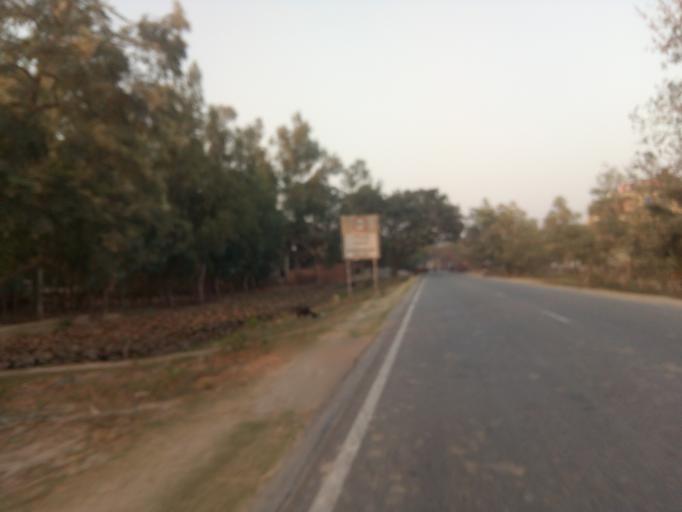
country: BD
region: Rajshahi
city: Bogra
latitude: 24.6433
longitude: 89.2534
